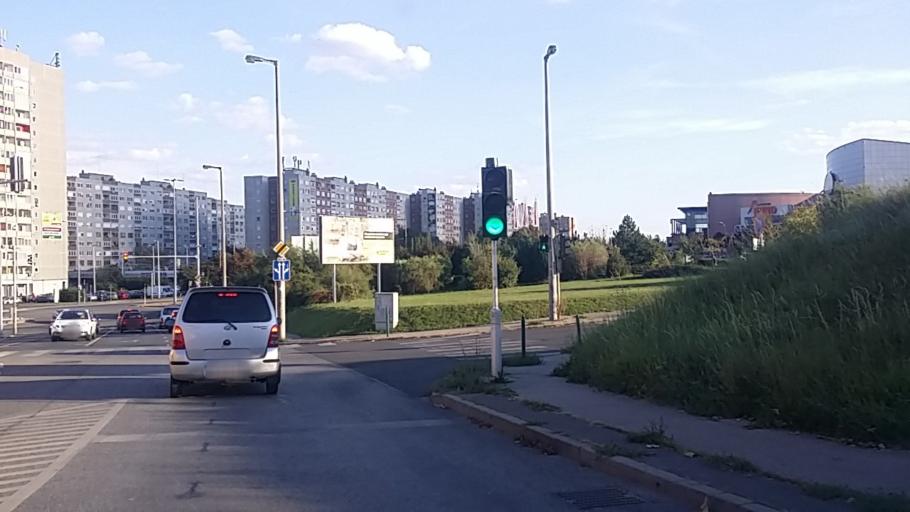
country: HU
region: Budapest
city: Budapest III. keruelet
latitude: 47.5487
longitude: 19.0277
